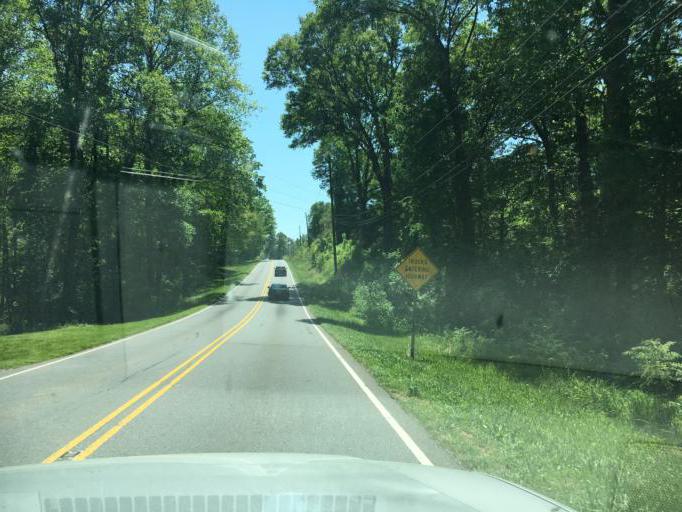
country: US
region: North Carolina
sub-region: Cleveland County
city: Shelby
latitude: 35.2483
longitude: -81.5665
